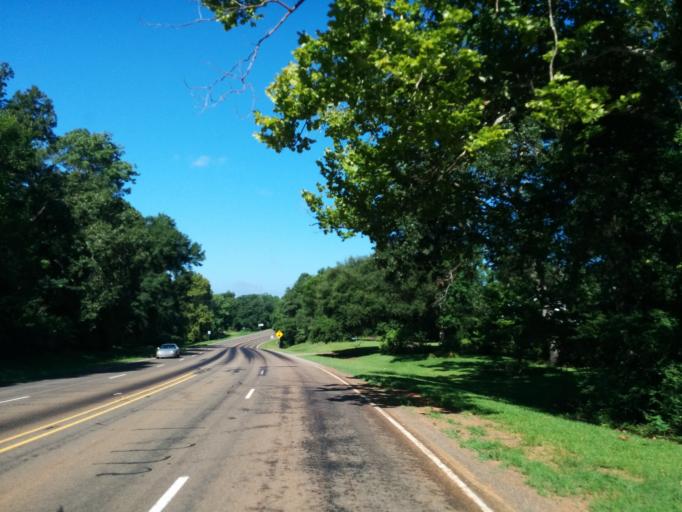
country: US
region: Texas
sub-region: Sabine County
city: Milam
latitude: 31.4338
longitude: -93.8413
